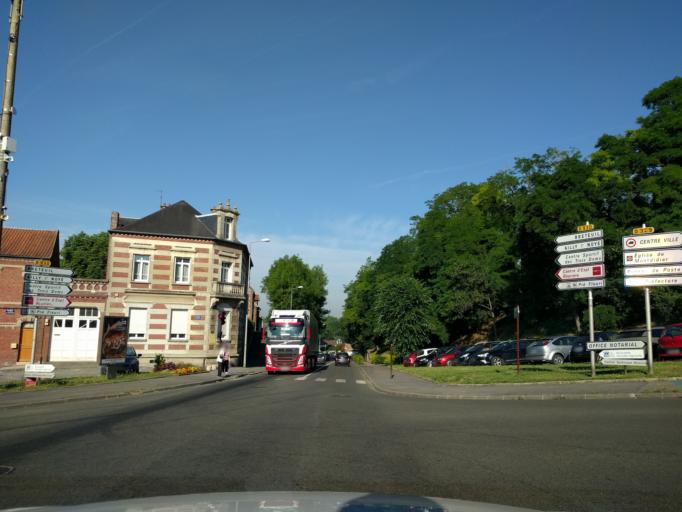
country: FR
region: Picardie
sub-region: Departement de la Somme
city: Montdidier
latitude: 49.6453
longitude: 2.5680
